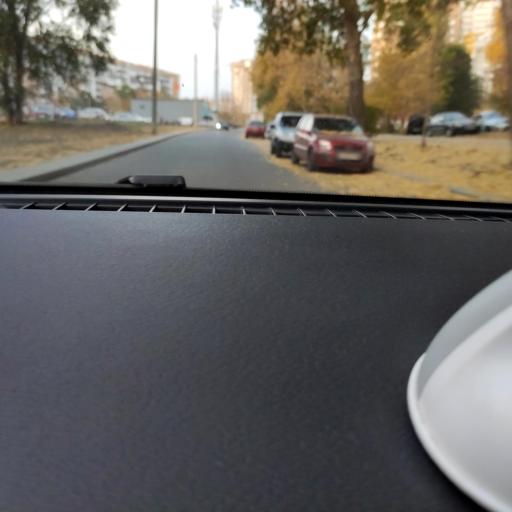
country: RU
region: Samara
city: Samara
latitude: 53.1905
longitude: 50.1366
